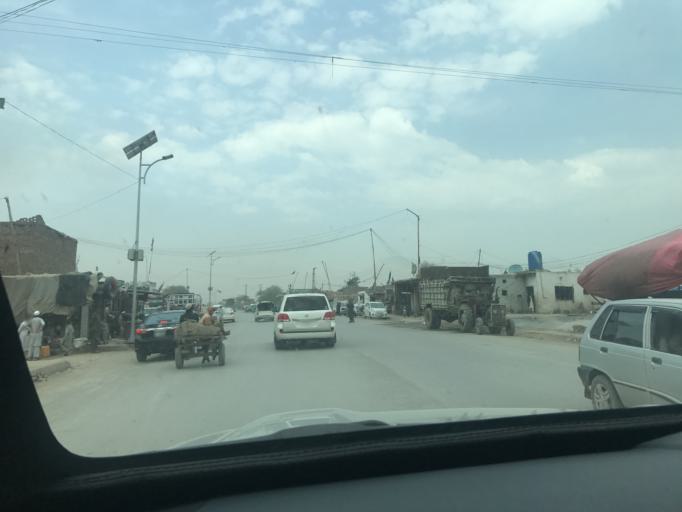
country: PK
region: Khyber Pakhtunkhwa
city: Peshawar
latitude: 33.9993
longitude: 71.4138
